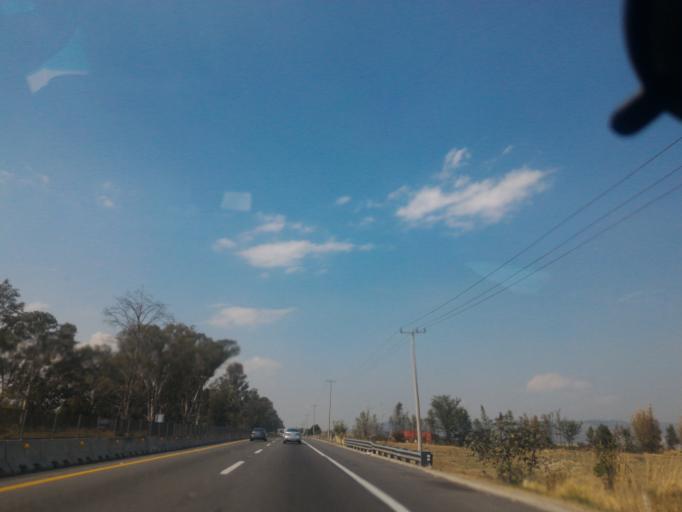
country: MX
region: Jalisco
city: Zapotiltic
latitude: 19.5863
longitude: -103.4498
